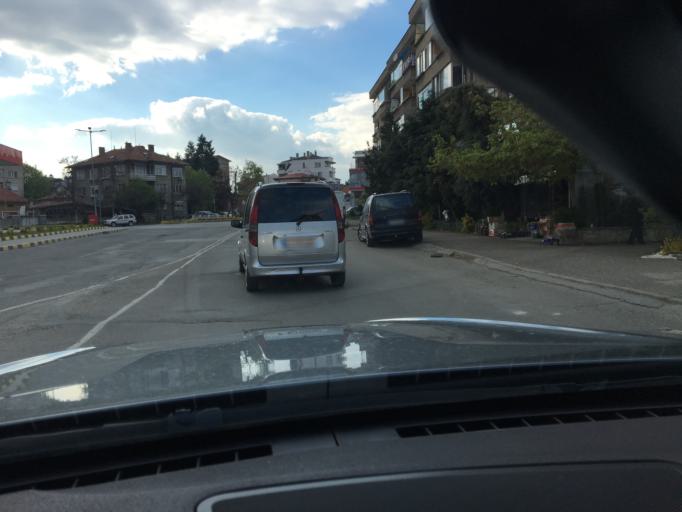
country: BG
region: Stara Zagora
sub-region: Obshtina Kazanluk
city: Kazanluk
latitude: 42.6155
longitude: 25.3903
